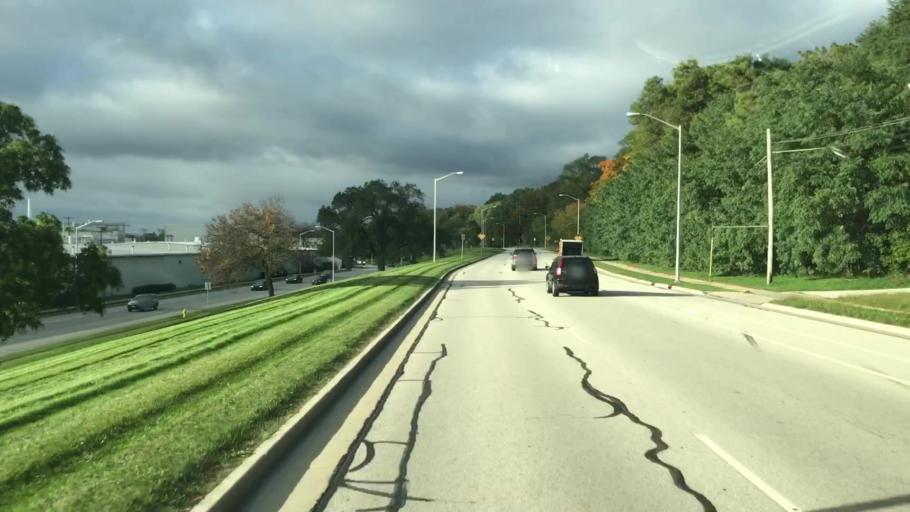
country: US
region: Wisconsin
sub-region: Waukesha County
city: Waukesha
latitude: 43.0211
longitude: -88.2256
